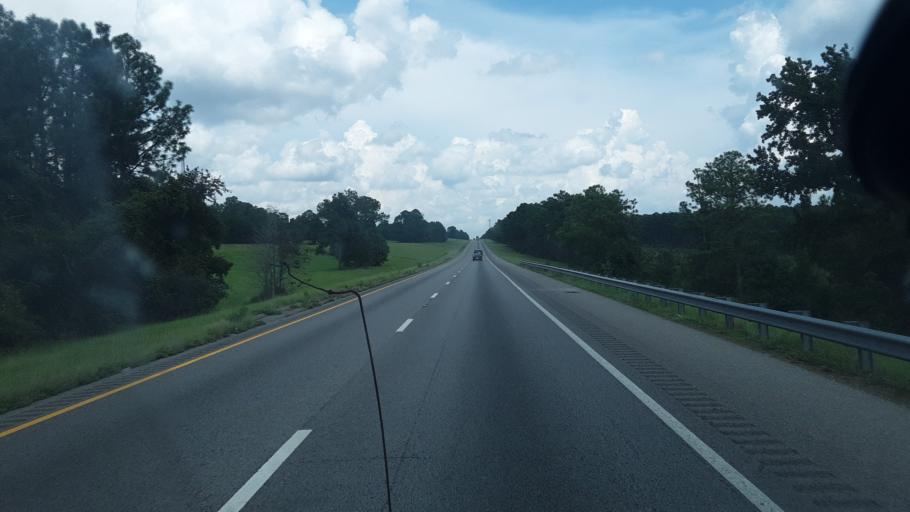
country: US
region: South Carolina
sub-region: Kershaw County
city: Elgin
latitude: 34.1598
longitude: -80.7257
